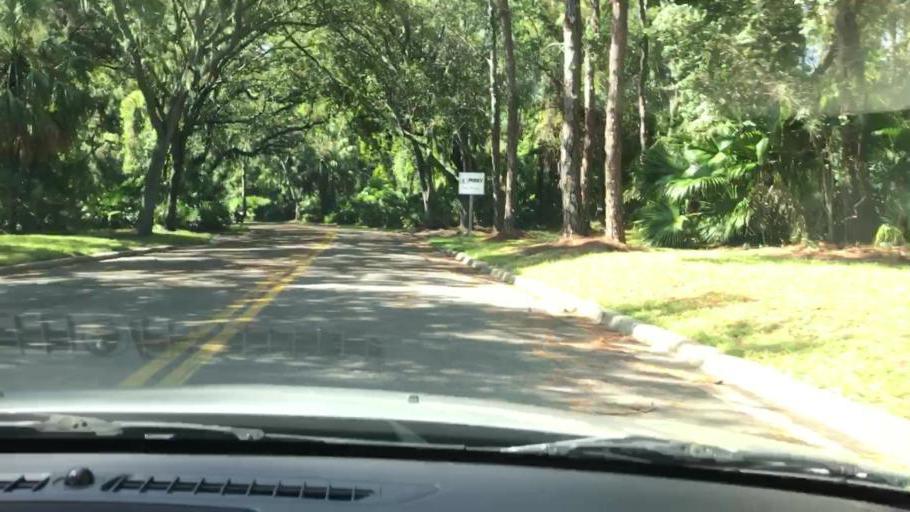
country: US
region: Florida
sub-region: Pinellas County
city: Bay Pines
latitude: 27.8134
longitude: -82.7694
